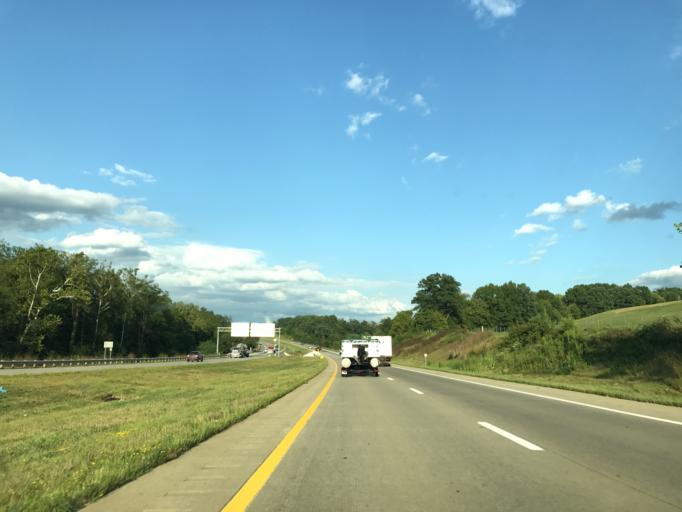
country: US
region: Ohio
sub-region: Wayne County
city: Wooster
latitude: 40.7983
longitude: -81.8908
